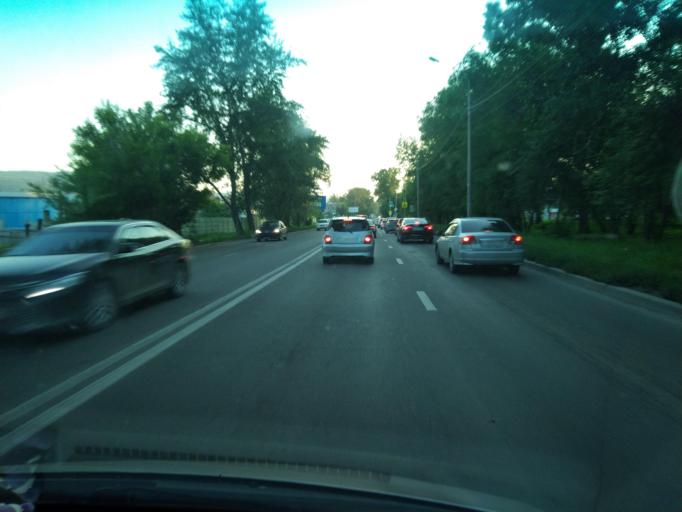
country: RU
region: Krasnoyarskiy
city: Krasnoyarsk
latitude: 55.9874
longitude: 92.9000
